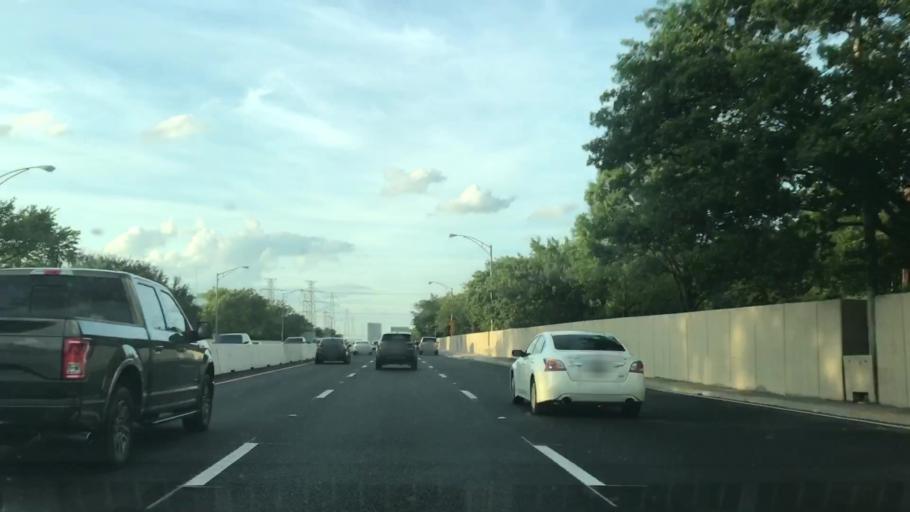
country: US
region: Texas
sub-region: Dallas County
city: University Park
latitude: 32.8983
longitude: -96.8104
